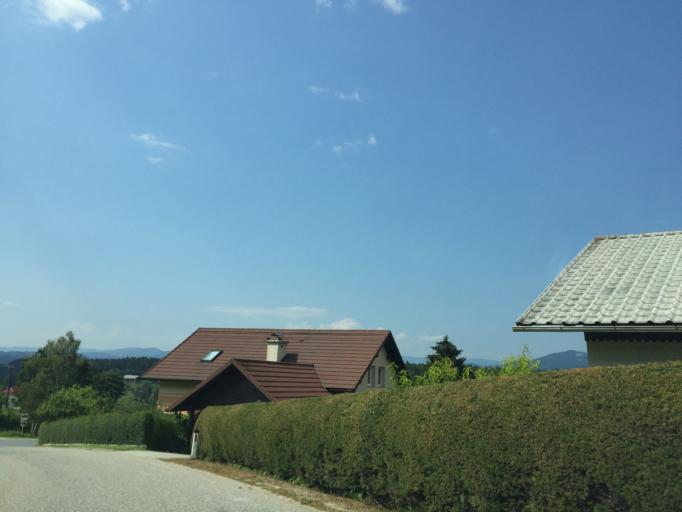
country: SI
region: Slovenj Gradec
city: Smartno pri Slovenj Gradcu
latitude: 46.4509
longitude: 15.1202
